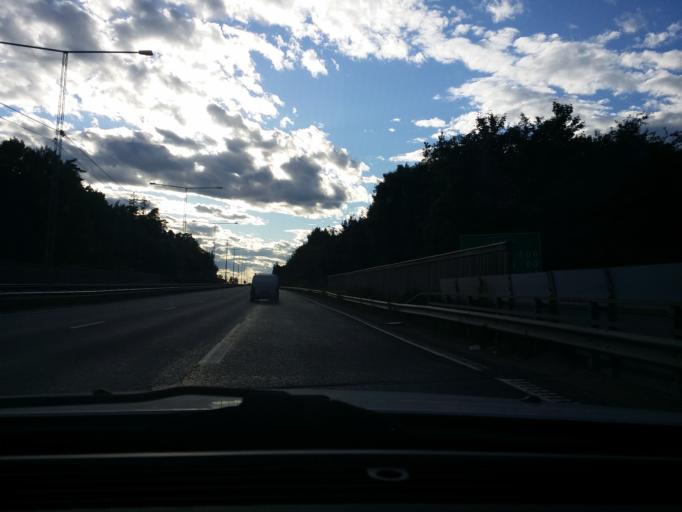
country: SE
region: Stockholm
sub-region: Upplands-Bro Kommun
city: Kungsaengen
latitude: 59.4744
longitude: 17.8045
